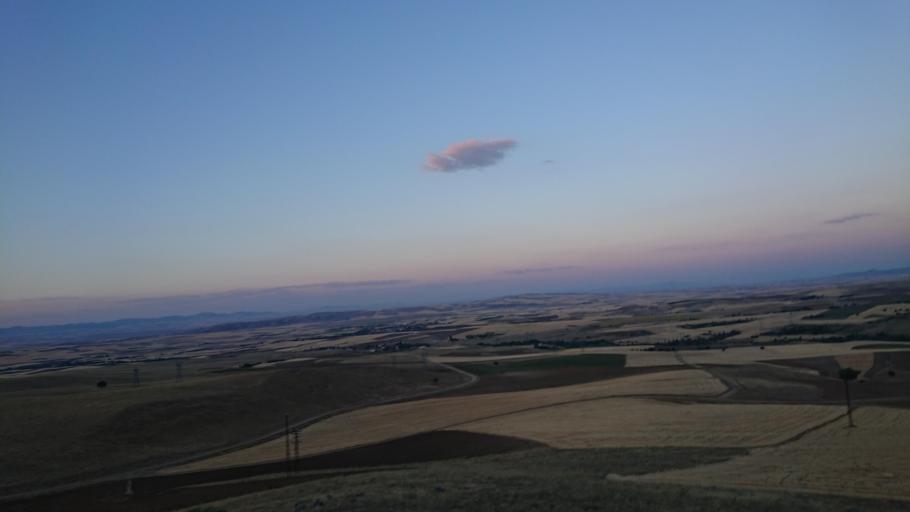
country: TR
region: Aksaray
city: Agacoren
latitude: 38.9124
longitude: 33.8925
